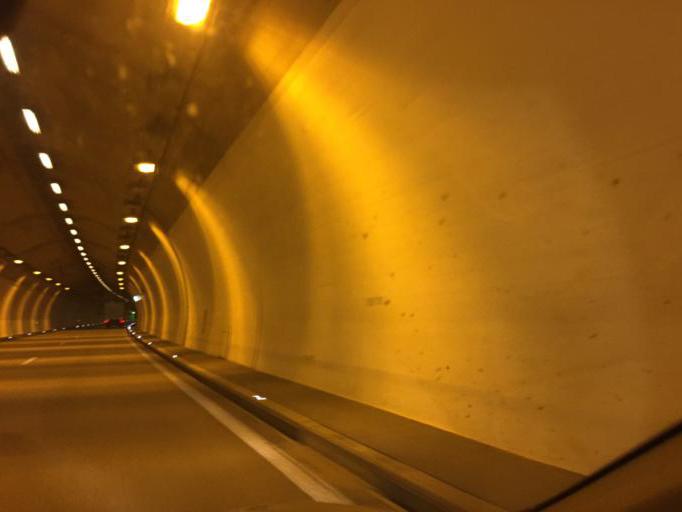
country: LU
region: Luxembourg
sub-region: Canton de Mersch
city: Lintgen
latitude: 49.7092
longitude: 6.1186
